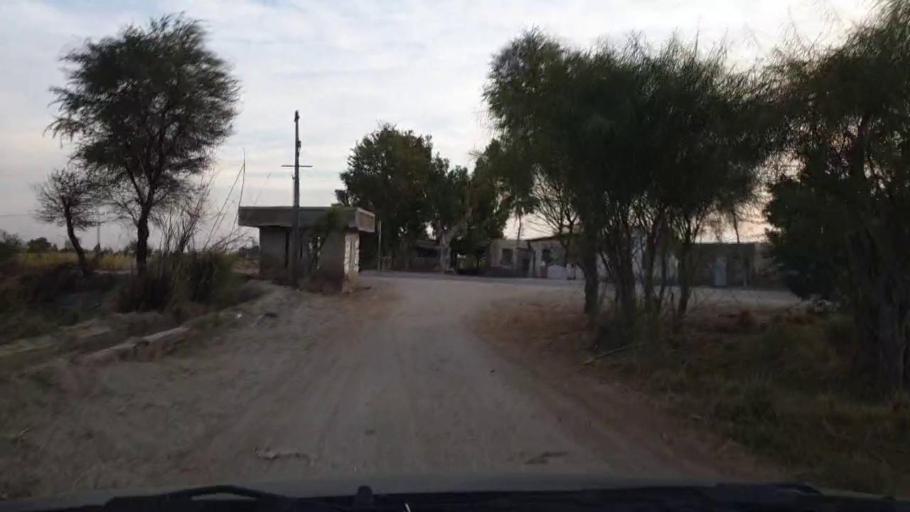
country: PK
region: Sindh
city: Khadro
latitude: 26.1256
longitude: 68.7779
